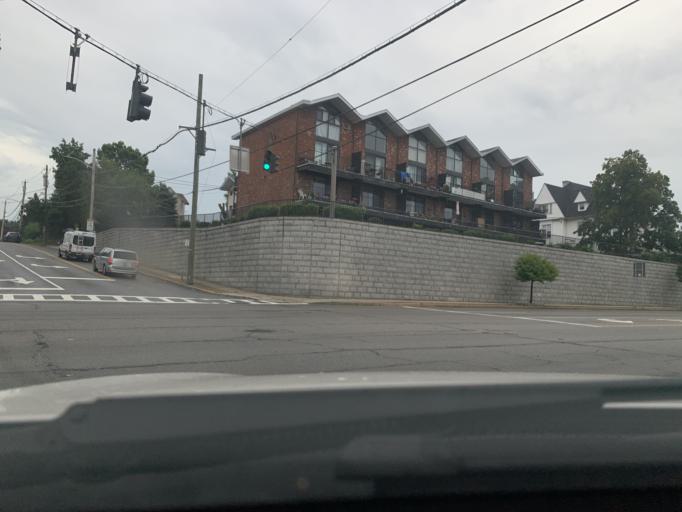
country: US
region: New York
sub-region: Westchester County
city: Ossining
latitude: 41.1588
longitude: -73.8611
